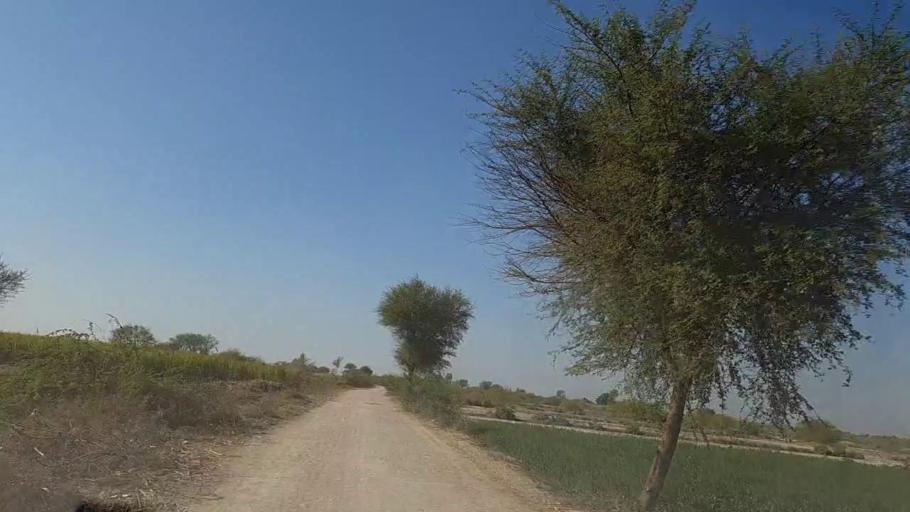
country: PK
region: Sindh
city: Digri
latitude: 25.1915
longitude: 68.9963
